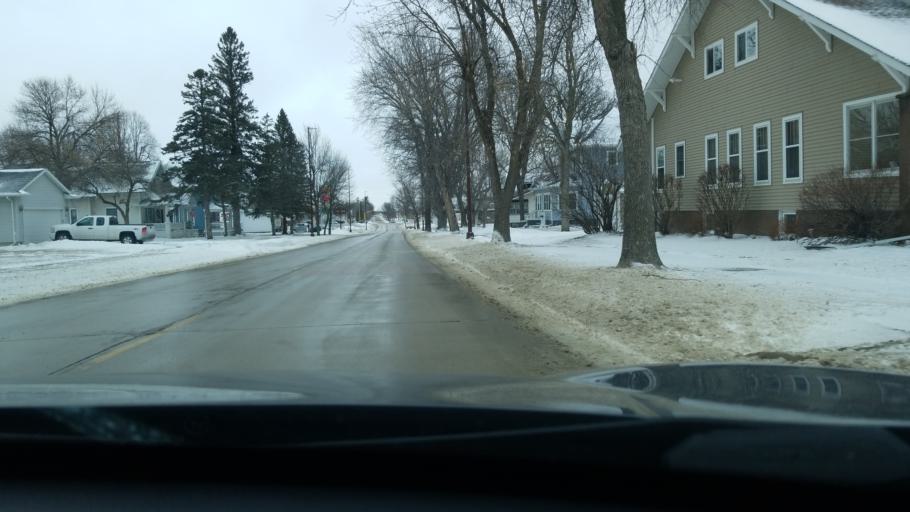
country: US
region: Iowa
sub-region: Lyon County
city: Rock Rapids
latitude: 43.4286
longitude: -96.1755
